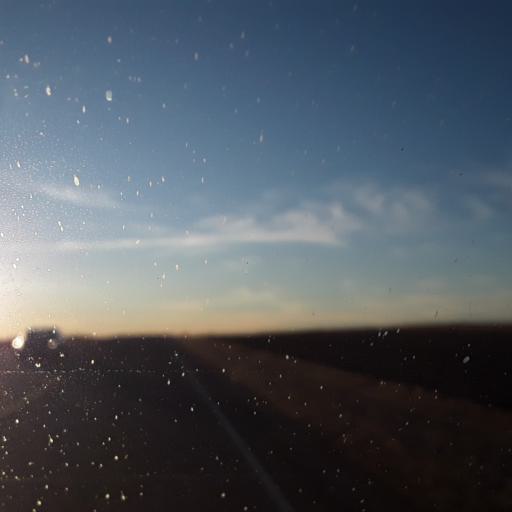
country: US
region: Colorado
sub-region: Cheyenne County
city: Cheyenne Wells
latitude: 38.8368
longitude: -102.2819
